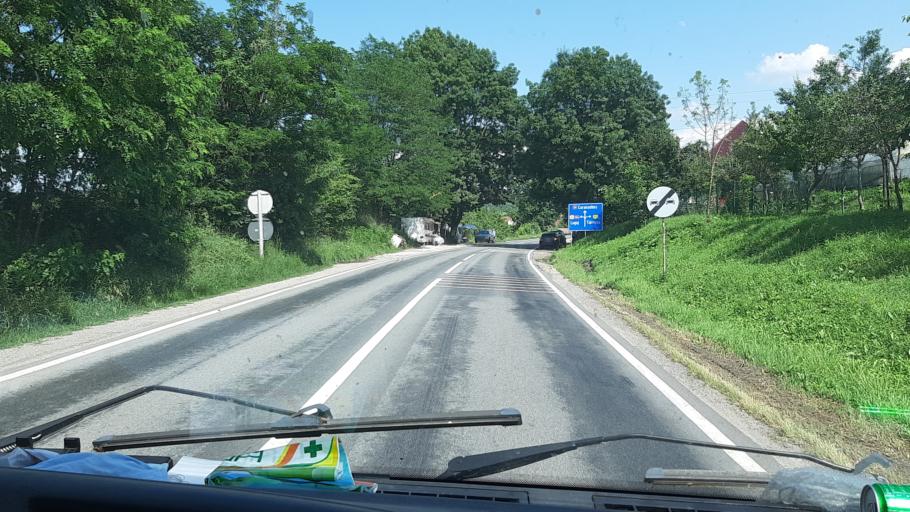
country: RO
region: Caras-Severin
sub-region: Comuna Ezeris
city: Ezeris
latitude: 45.3773
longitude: 21.9339
